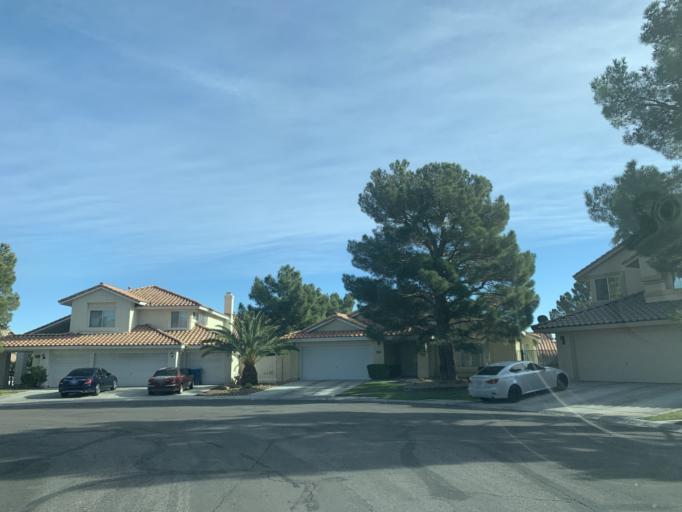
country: US
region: Nevada
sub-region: Clark County
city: Spring Valley
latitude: 36.1281
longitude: -115.2858
